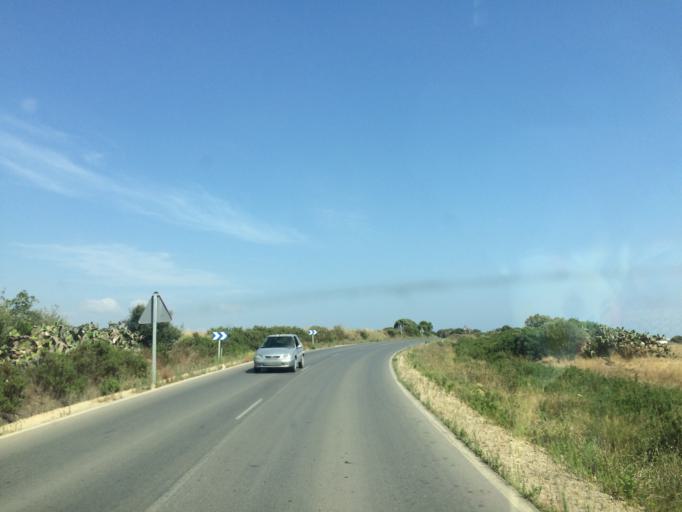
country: ES
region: Andalusia
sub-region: Provincia de Cadiz
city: Conil de la Frontera
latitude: 36.2378
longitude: -6.0537
